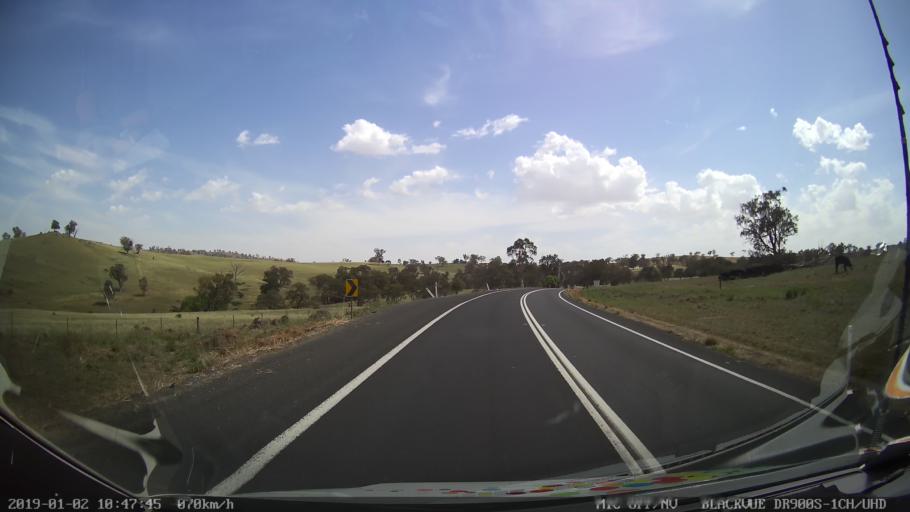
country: AU
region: New South Wales
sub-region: Cootamundra
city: Cootamundra
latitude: -34.7418
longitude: 148.2719
